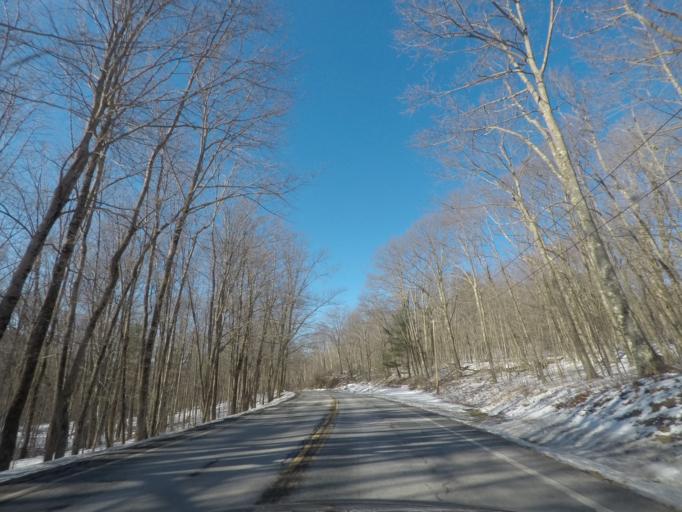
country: US
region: Massachusetts
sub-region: Berkshire County
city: West Stockbridge
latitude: 42.3404
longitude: -73.4729
